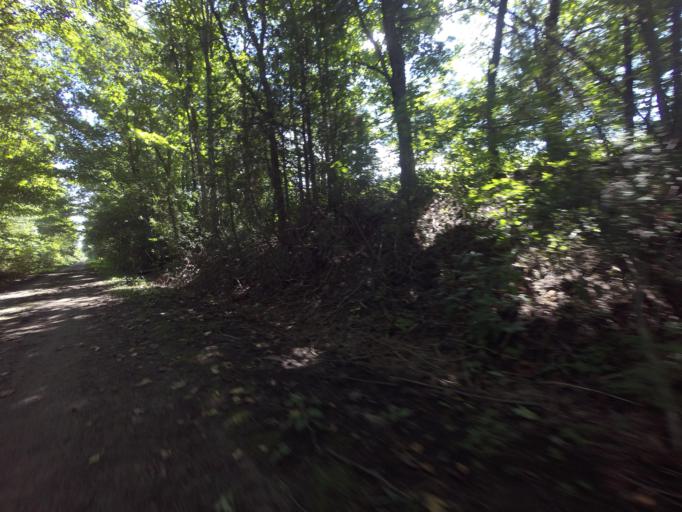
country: CA
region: Ontario
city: Orangeville
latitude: 43.7929
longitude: -80.3020
